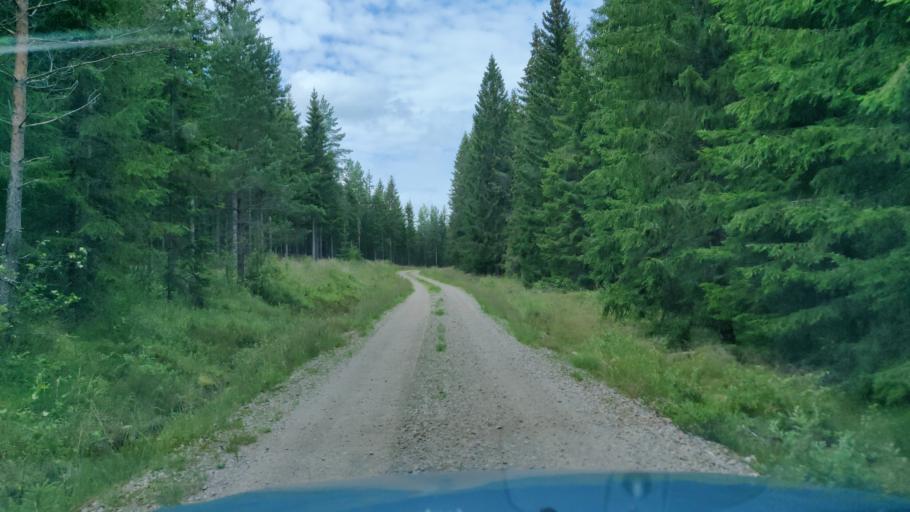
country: SE
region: Vaermland
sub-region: Hagfors Kommun
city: Hagfors
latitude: 59.9574
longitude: 13.5902
